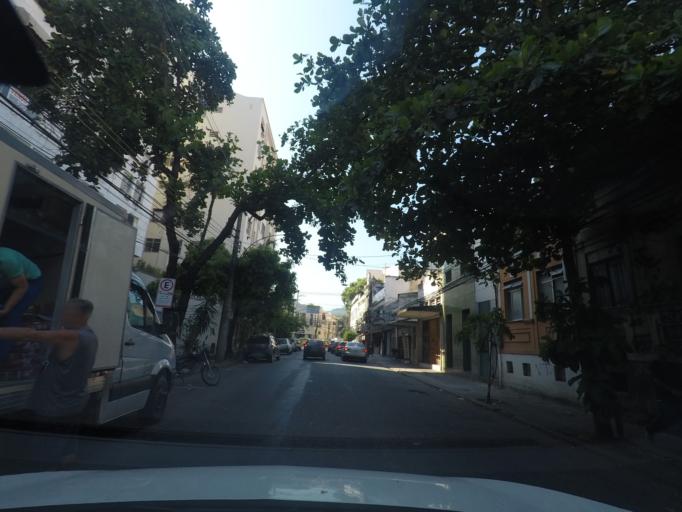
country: BR
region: Rio de Janeiro
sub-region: Rio De Janeiro
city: Rio de Janeiro
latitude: -22.9171
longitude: -43.2121
